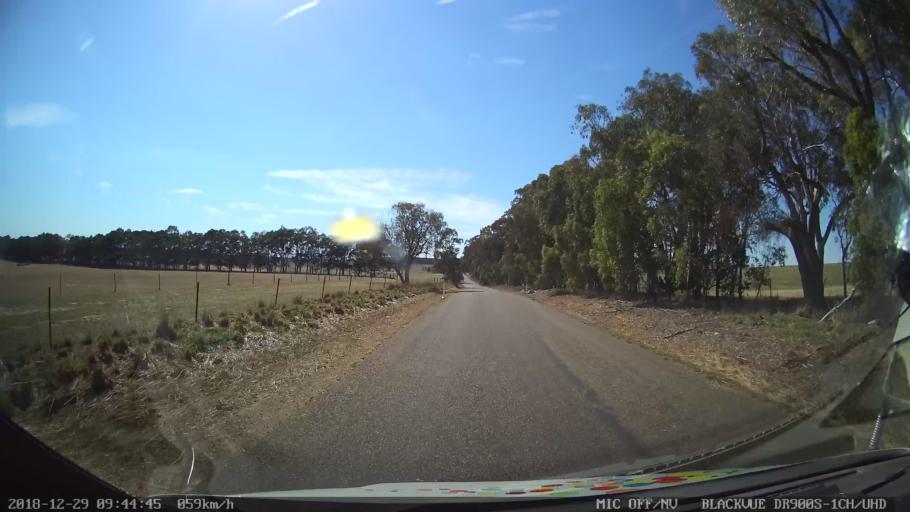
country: AU
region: New South Wales
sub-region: Upper Lachlan Shire
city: Crookwell
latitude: -34.6916
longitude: 149.4283
